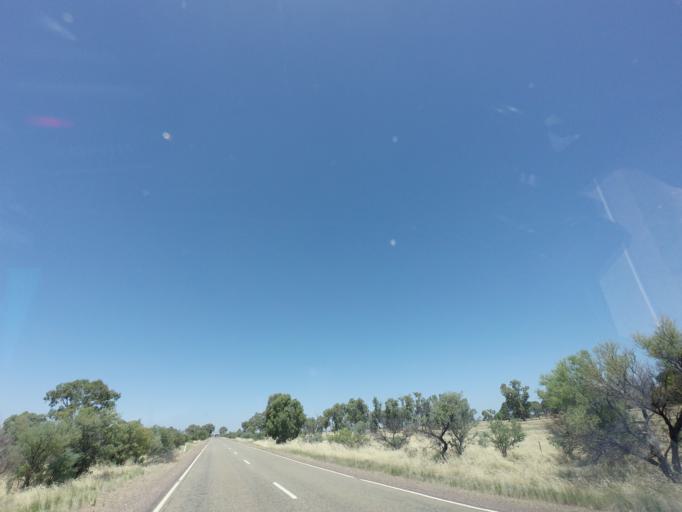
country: AU
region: South Australia
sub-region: Flinders Ranges
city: Quorn
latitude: -32.6663
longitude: 138.1565
